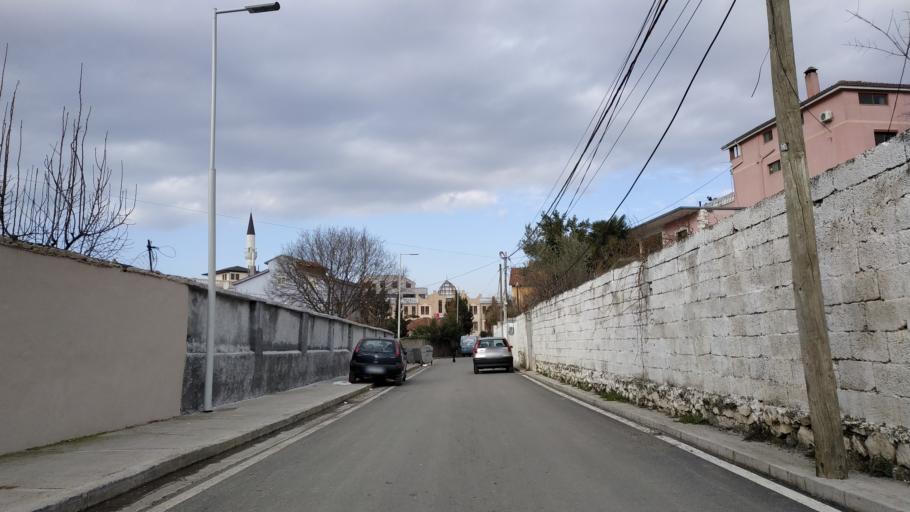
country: AL
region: Shkoder
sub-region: Rrethi i Shkodres
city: Shkoder
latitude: 42.0555
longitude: 19.5031
